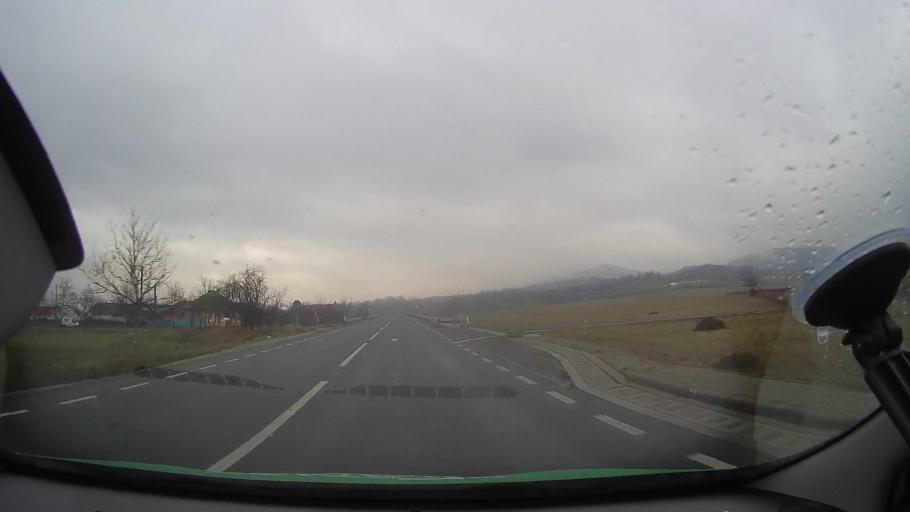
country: RO
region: Hunedoara
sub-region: Comuna Baia de Cris
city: Baia de Cris
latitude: 46.1758
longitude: 22.7080
